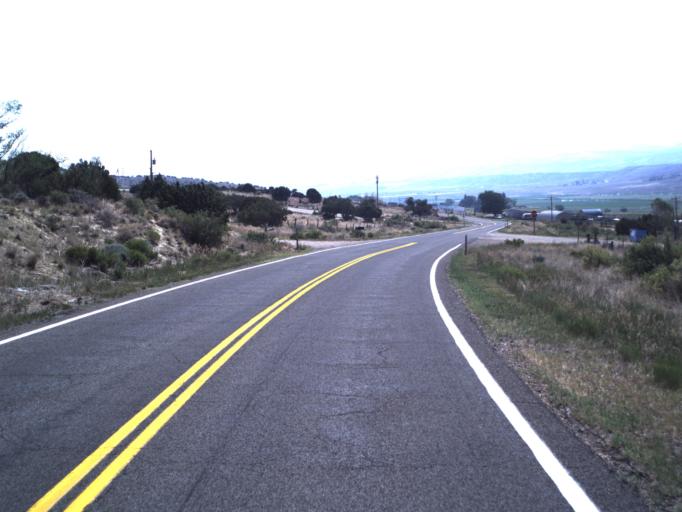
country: US
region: Utah
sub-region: Daggett County
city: Manila
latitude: 40.9783
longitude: -109.7809
